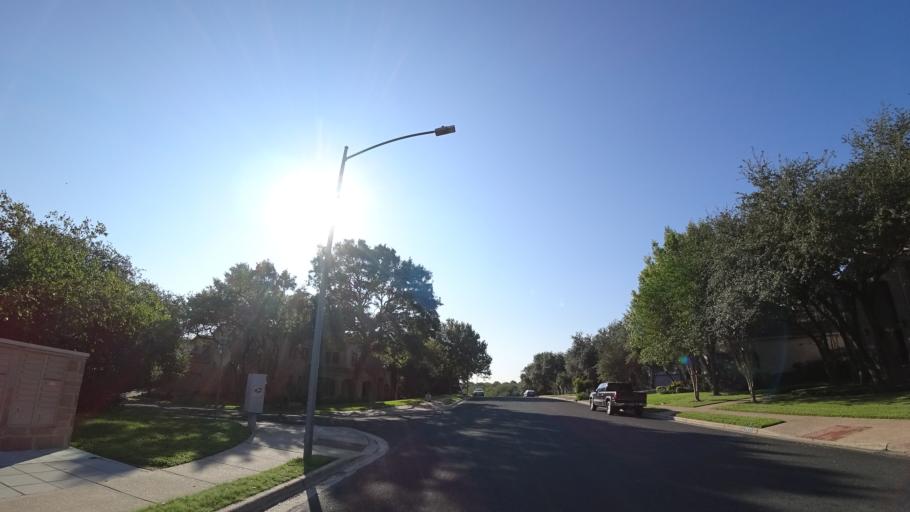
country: US
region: Texas
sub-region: Travis County
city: Rollingwood
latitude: 30.2684
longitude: -97.7952
